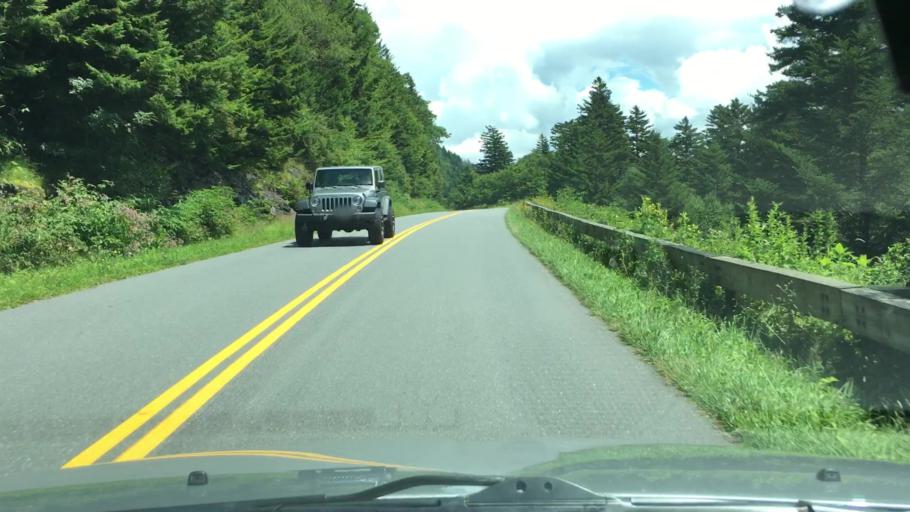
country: US
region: North Carolina
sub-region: Buncombe County
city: Black Mountain
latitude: 35.7345
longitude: -82.3206
